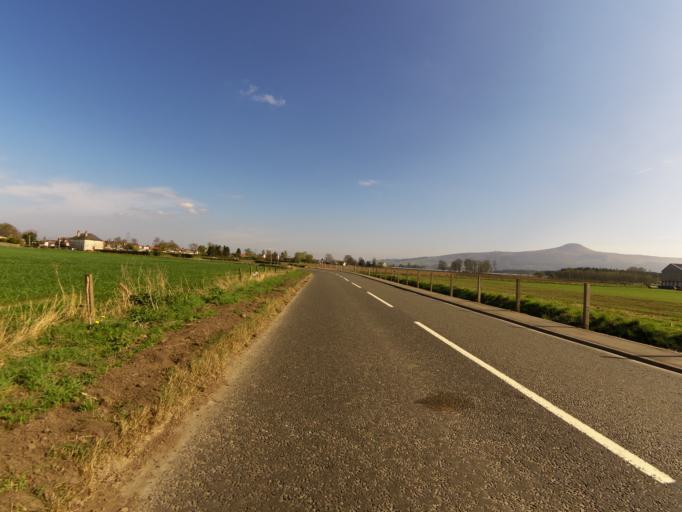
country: GB
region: Scotland
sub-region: Fife
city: Auchtermuchty
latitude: 56.2824
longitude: -3.2194
